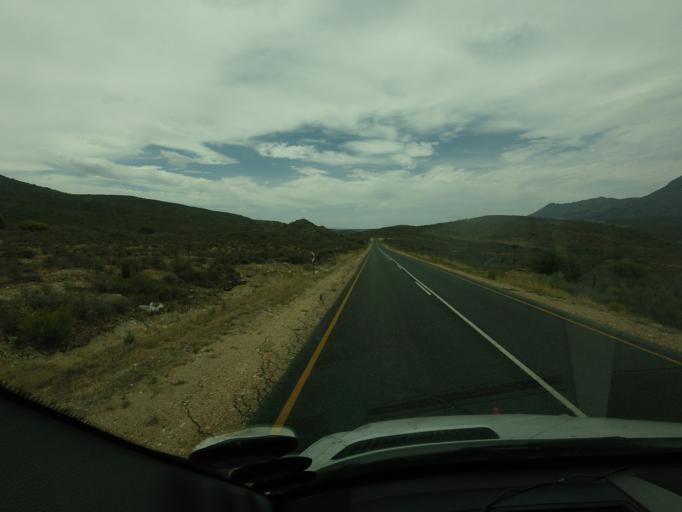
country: ZA
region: Western Cape
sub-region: Overberg District Municipality
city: Swellendam
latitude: -33.8606
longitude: 20.7782
